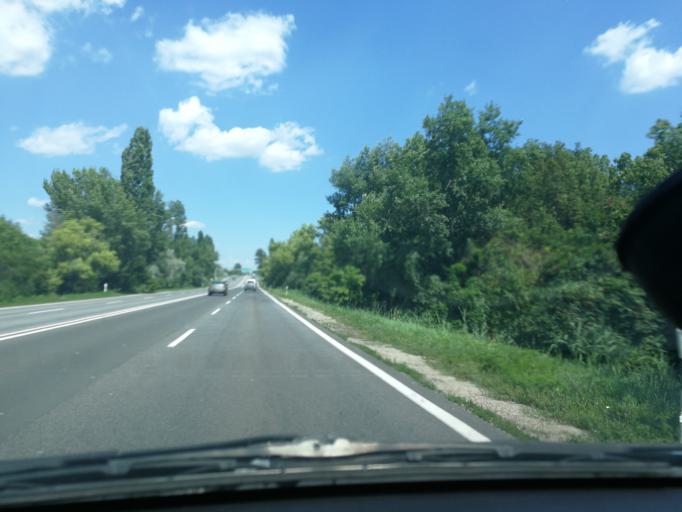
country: HU
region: Fejer
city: Szekesfehervar
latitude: 47.2086
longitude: 18.3926
